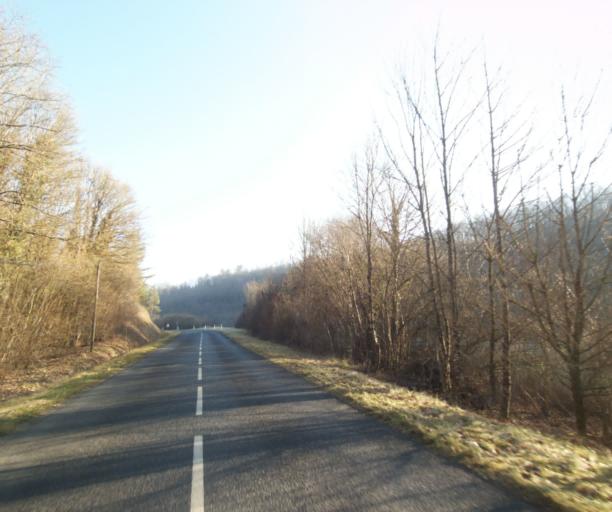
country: FR
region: Champagne-Ardenne
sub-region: Departement de la Haute-Marne
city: Chevillon
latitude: 48.5260
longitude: 5.1586
